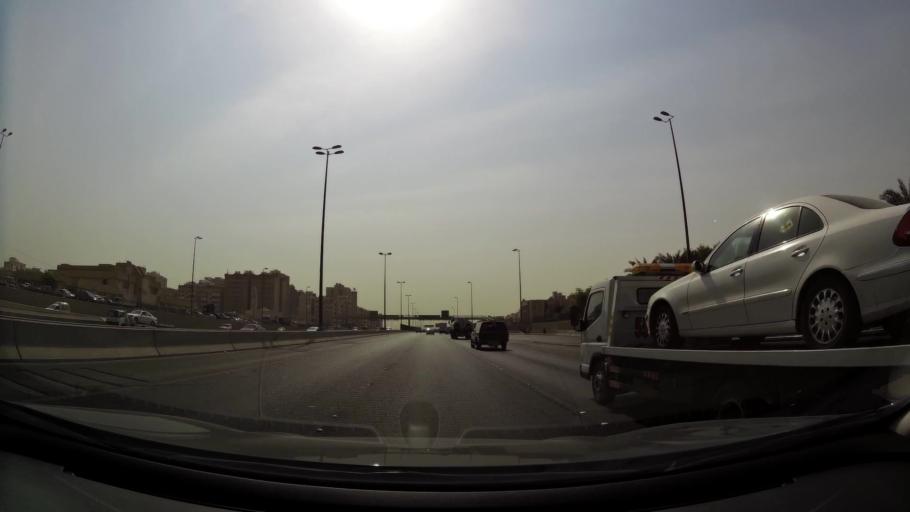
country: KW
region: Al Farwaniyah
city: Al Farwaniyah
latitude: 29.2753
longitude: 47.9502
